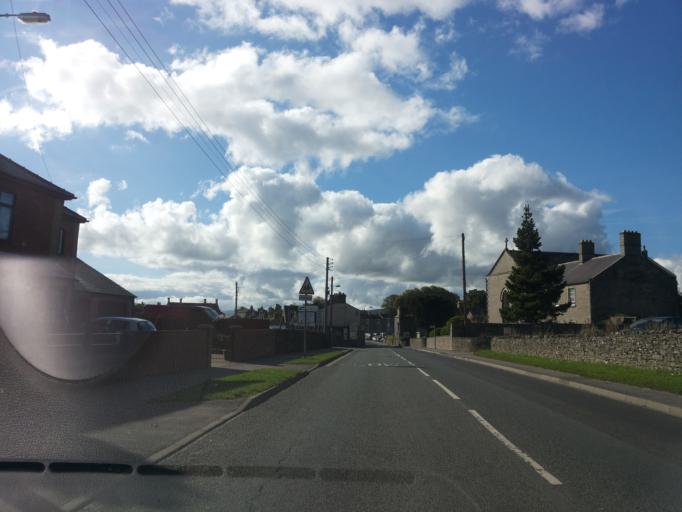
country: GB
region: England
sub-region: North Yorkshire
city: Leyburn
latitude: 54.3123
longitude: -1.8278
